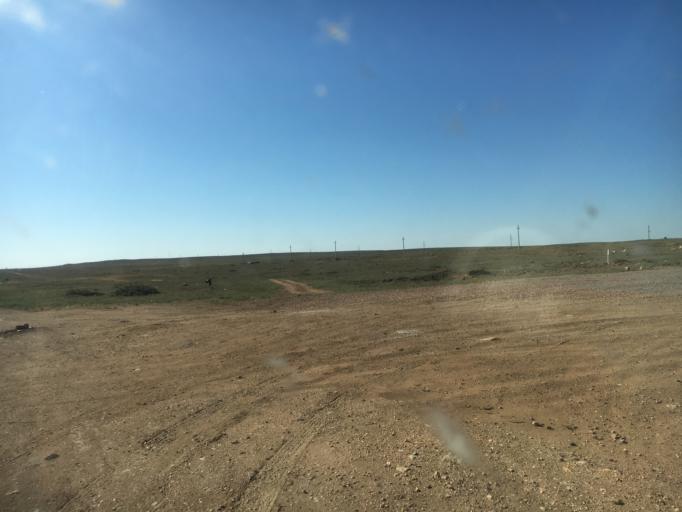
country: RU
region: Orenburg
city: Dombarovskiy
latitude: 50.0818
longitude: 59.5689
